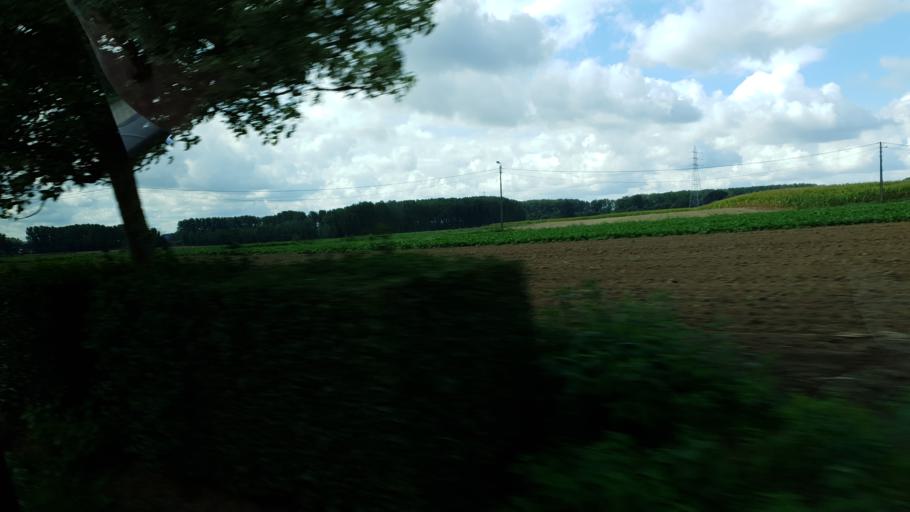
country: BE
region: Wallonia
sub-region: Province du Hainaut
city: Pecq
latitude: 50.6480
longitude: 3.3391
